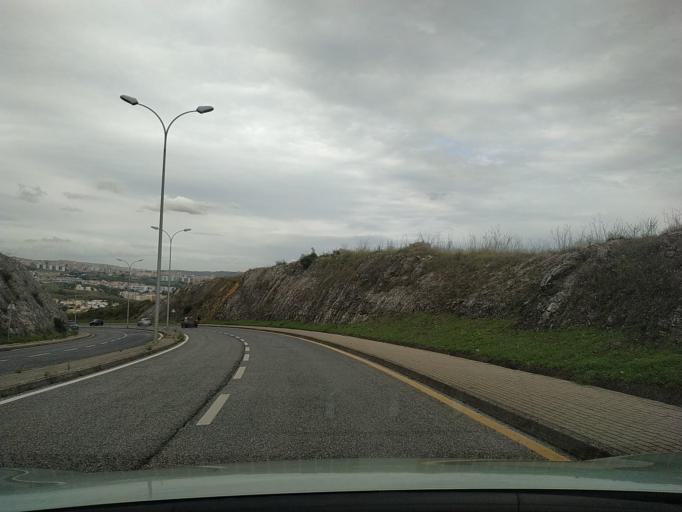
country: PT
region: Lisbon
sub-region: Amadora
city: Amadora
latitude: 38.7714
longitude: -9.2235
